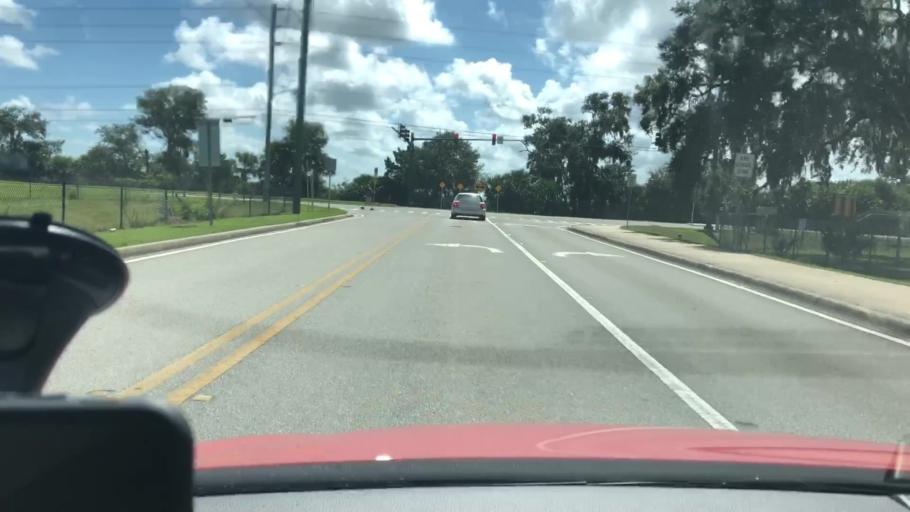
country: US
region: Florida
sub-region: Volusia County
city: New Smyrna Beach
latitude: 29.0033
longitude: -80.9220
